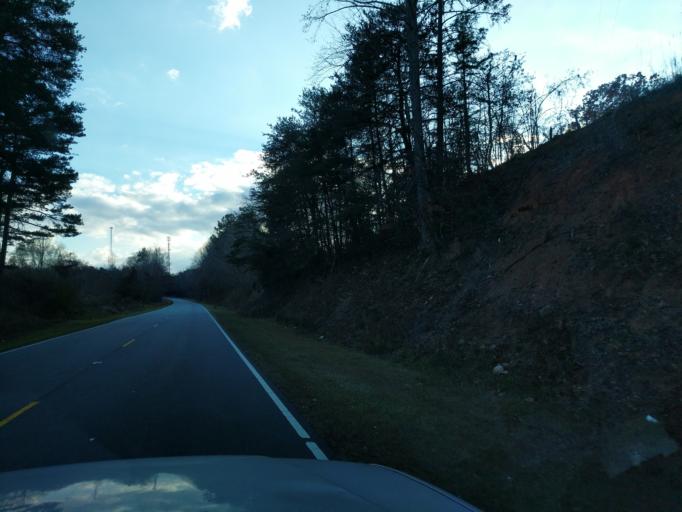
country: US
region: North Carolina
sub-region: Rutherford County
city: Rutherfordton
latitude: 35.5048
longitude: -81.9758
